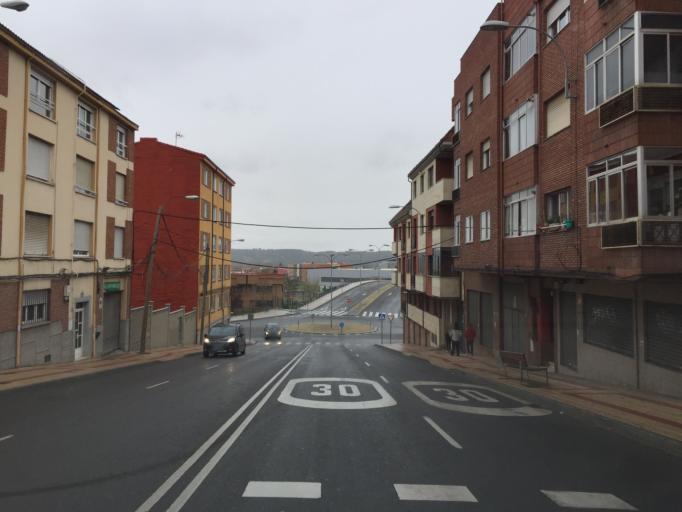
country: ES
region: Castille and Leon
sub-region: Provincia de Leon
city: Leon
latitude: 42.6149
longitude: -5.5697
